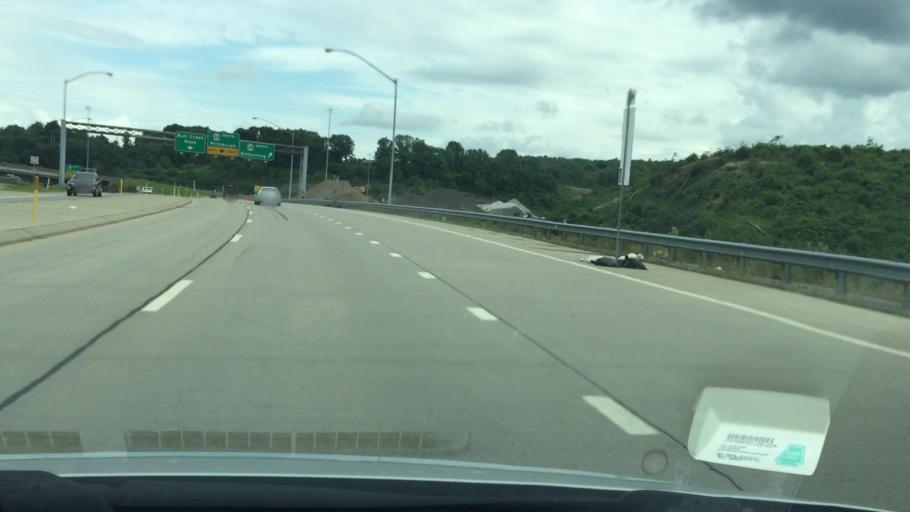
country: US
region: Pennsylvania
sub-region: Allegheny County
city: Tarentum
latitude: 40.6107
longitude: -79.7565
